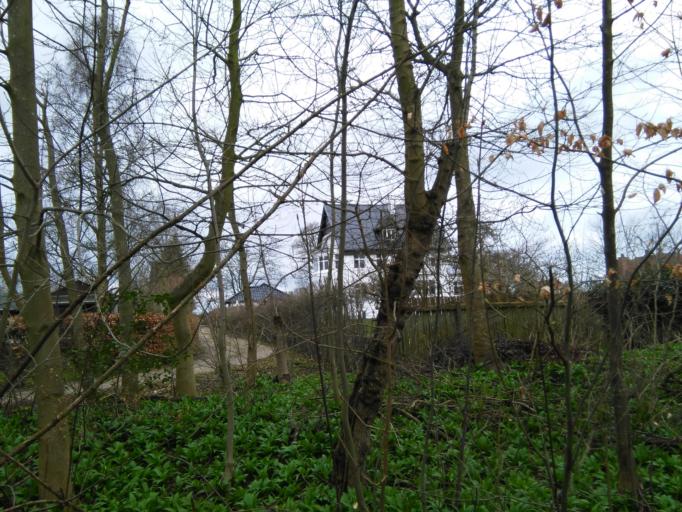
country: DK
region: Central Jutland
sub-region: Arhus Kommune
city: Arhus
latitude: 56.1822
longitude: 10.2228
